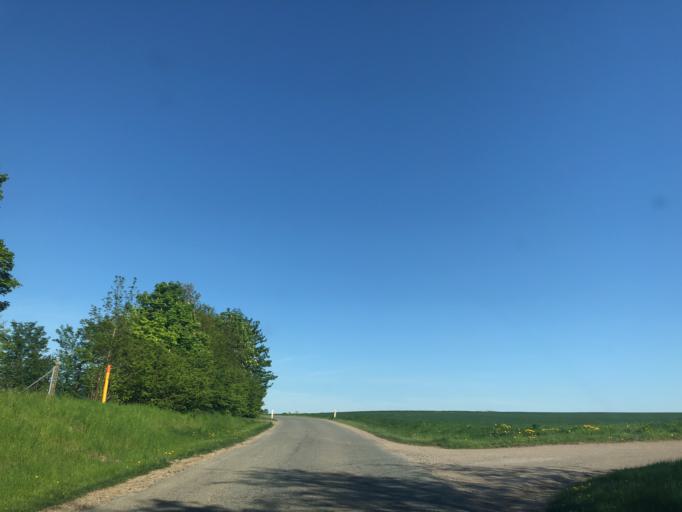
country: DK
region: Zealand
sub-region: Ringsted Kommune
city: Ringsted
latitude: 55.4512
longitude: 11.7089
